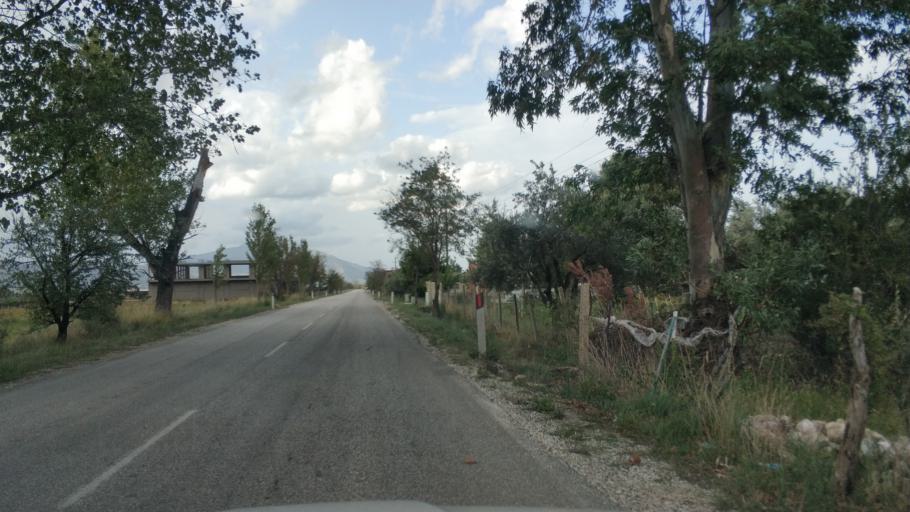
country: AL
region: Vlore
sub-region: Rrethi i Vlores
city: Orikum
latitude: 40.2840
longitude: 19.4986
